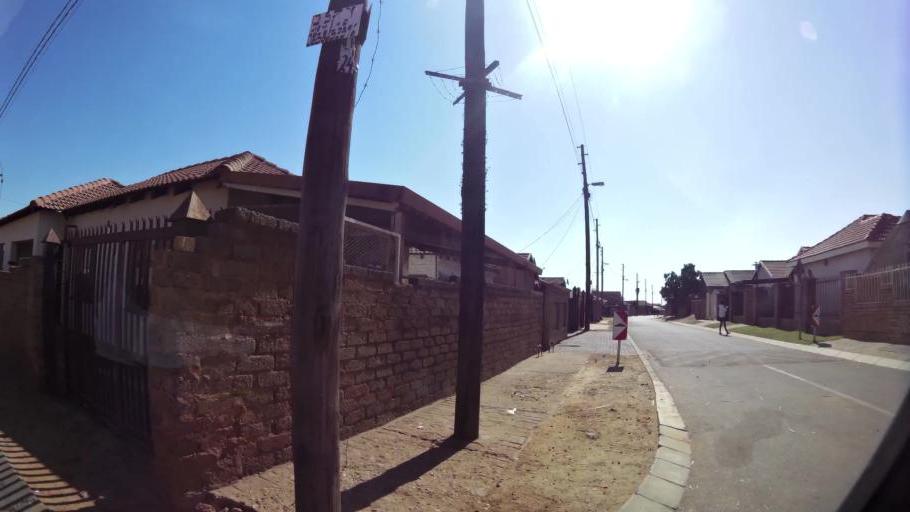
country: ZA
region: Gauteng
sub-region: City of Tshwane Metropolitan Municipality
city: Mabopane
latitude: -25.5548
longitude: 28.0734
